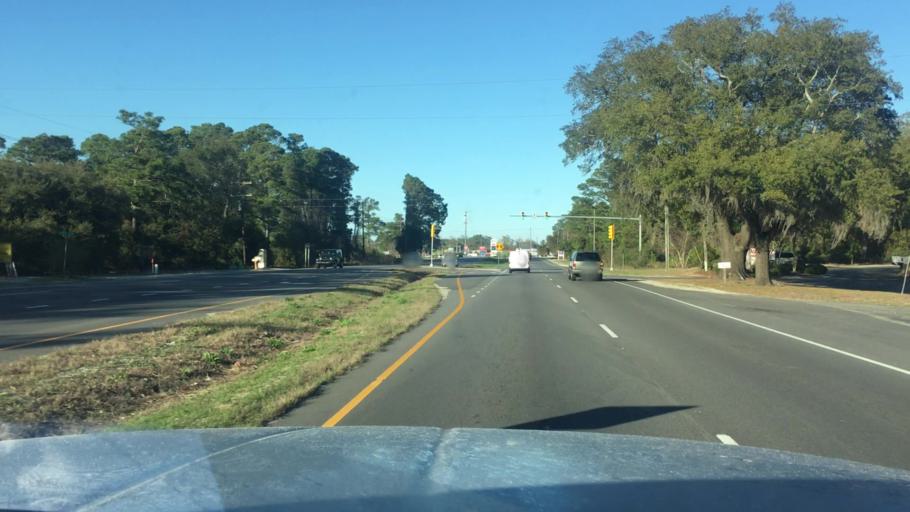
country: US
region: North Carolina
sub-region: New Hanover County
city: Myrtle Grove
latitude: 34.1306
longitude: -77.8967
